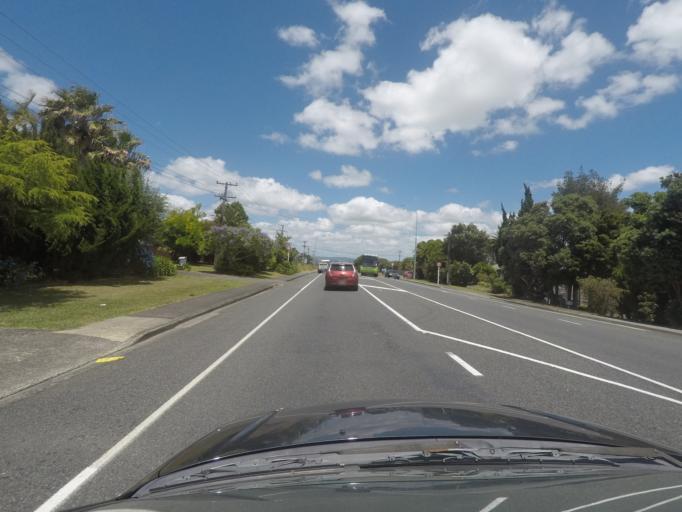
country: NZ
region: Northland
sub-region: Whangarei
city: Whangarei
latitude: -35.7493
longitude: 174.3676
